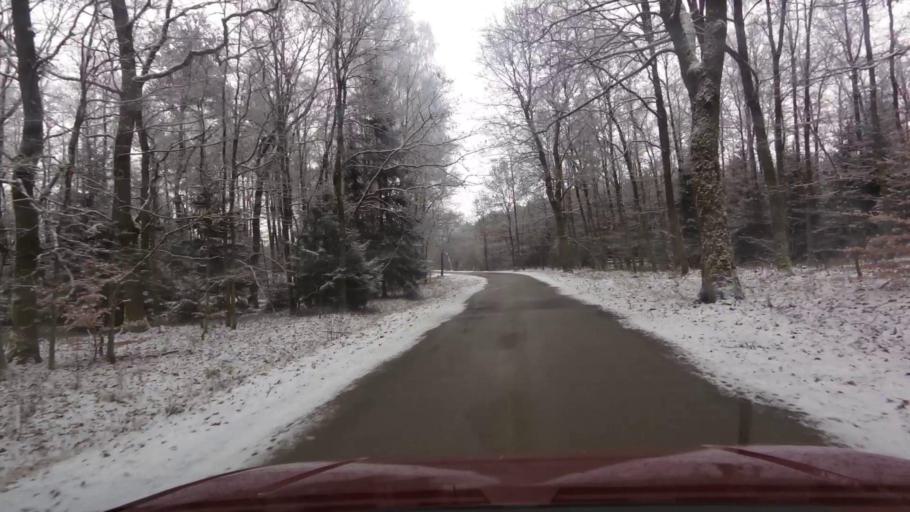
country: PL
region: West Pomeranian Voivodeship
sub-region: Powiat swidwinski
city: Polczyn-Zdroj
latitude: 53.7912
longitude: 16.0063
